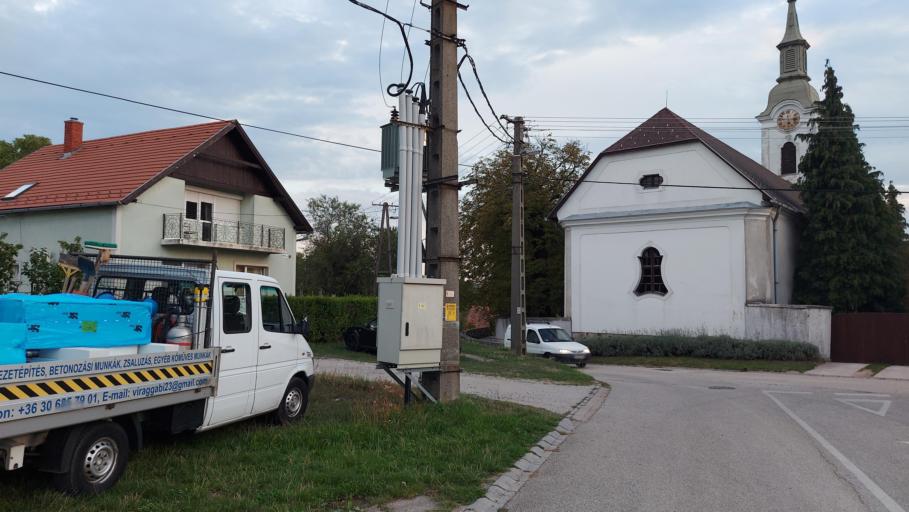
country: HU
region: Veszprem
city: Szentkiralyszabadja
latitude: 47.0581
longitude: 17.9706
